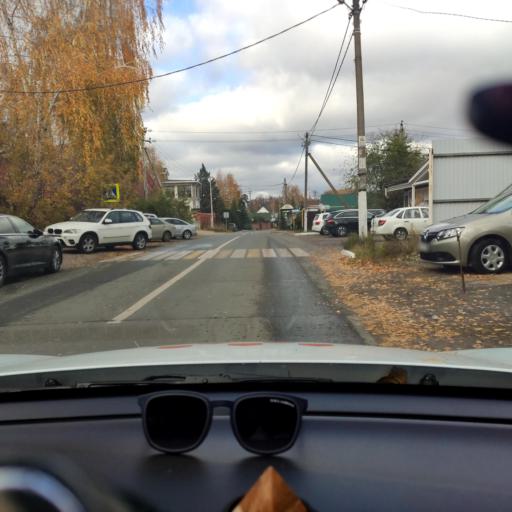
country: RU
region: Tatarstan
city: Verkhniy Uslon
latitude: 55.6212
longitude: 49.0141
